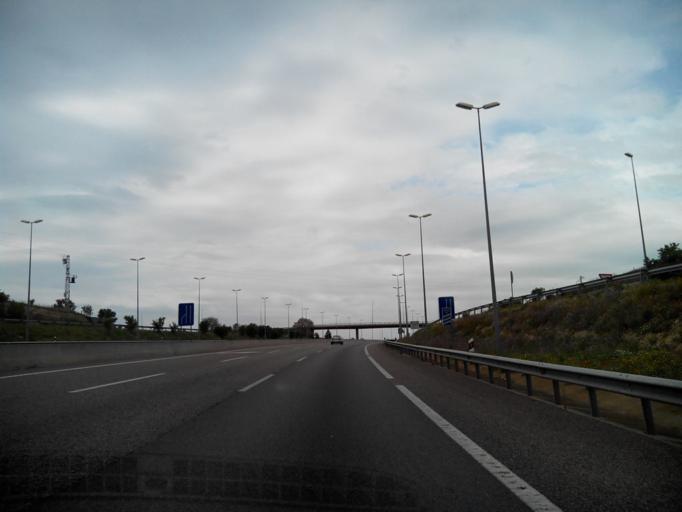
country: ES
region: Catalonia
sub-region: Provincia de Lleida
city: Cervera
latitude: 41.6702
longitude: 1.2221
